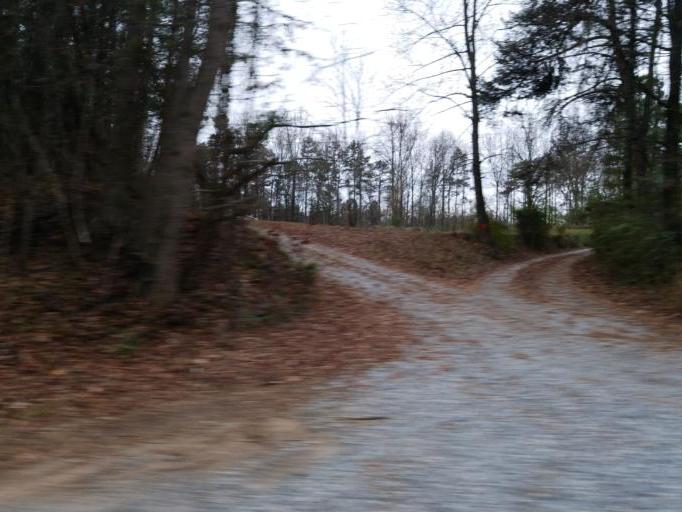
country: US
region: Georgia
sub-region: Dawson County
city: Dawsonville
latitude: 34.5054
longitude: -84.2105
